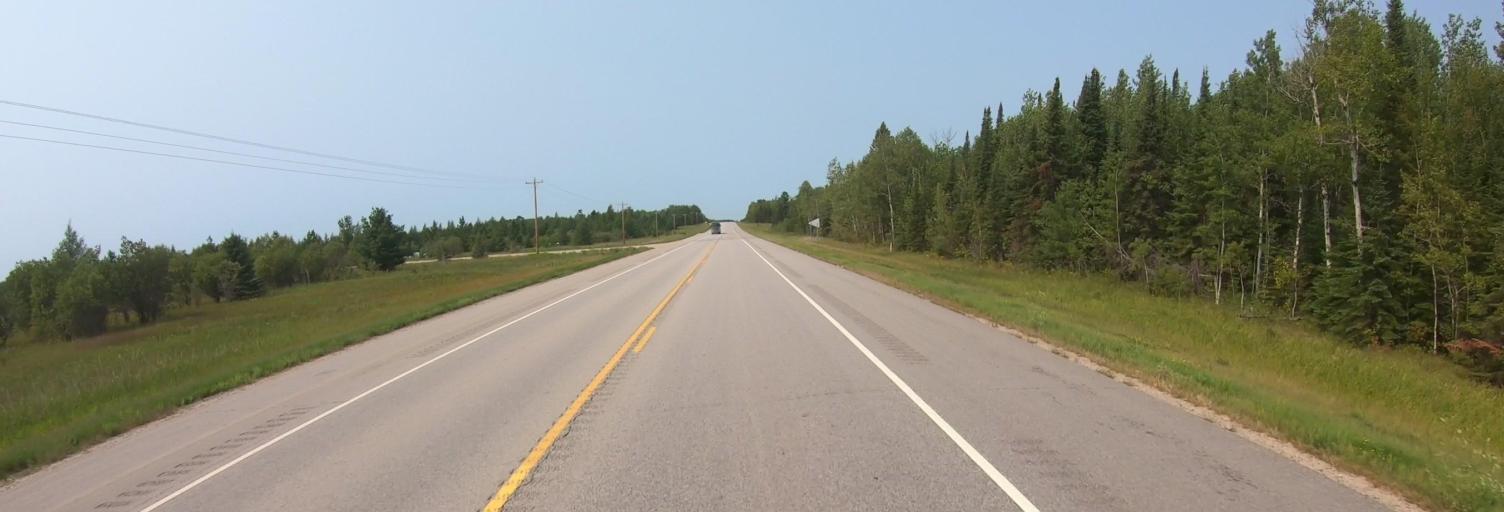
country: CA
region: Ontario
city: Fort Frances
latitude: 48.4103
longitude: -93.1608
